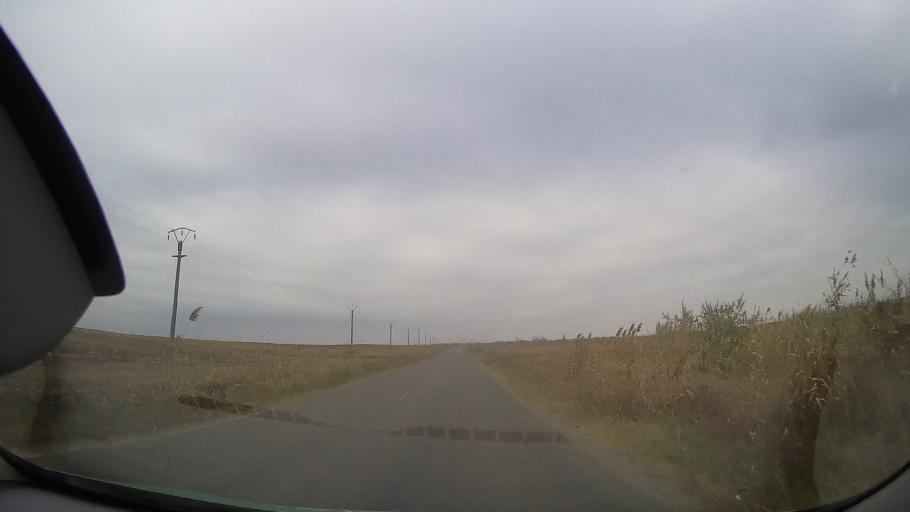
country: RO
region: Buzau
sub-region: Comuna Luciu
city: Luciu
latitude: 44.9667
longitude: 27.1122
